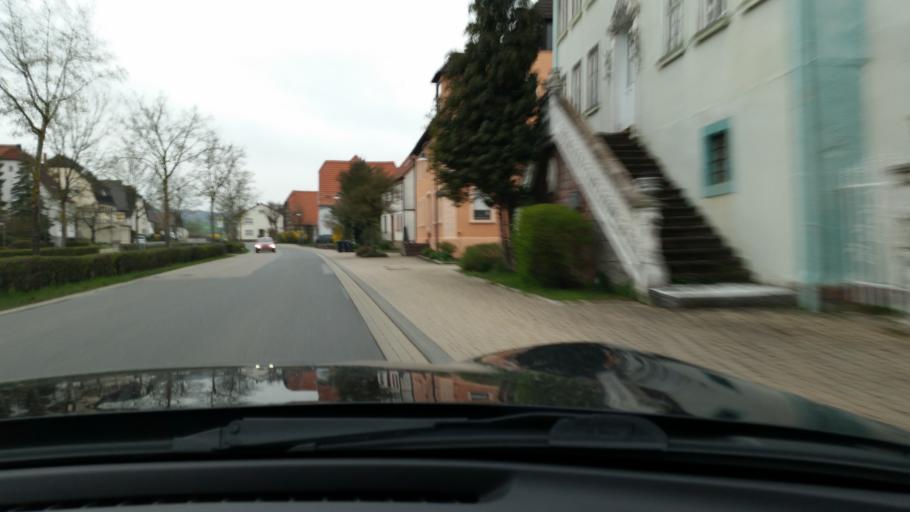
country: DE
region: Baden-Wuerttemberg
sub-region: Karlsruhe Region
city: Osterburken
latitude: 49.4724
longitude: 9.4112
